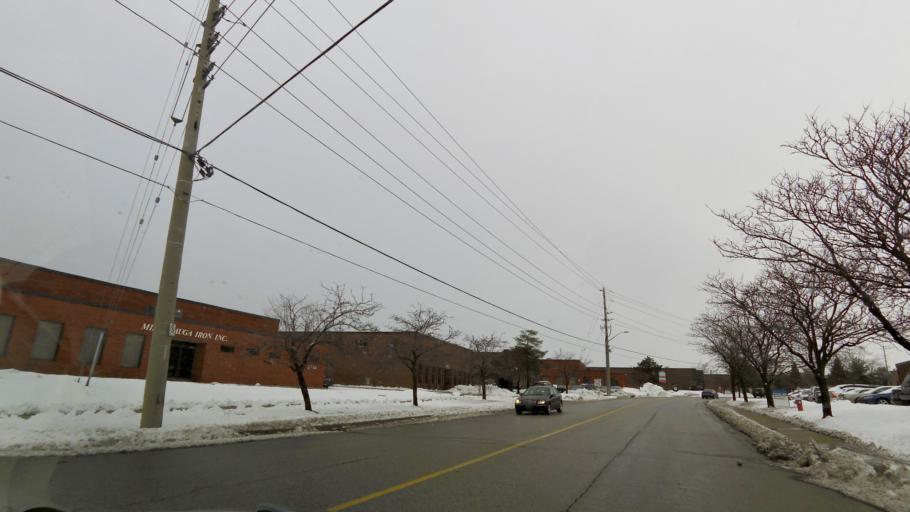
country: CA
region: Ontario
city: Mississauga
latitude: 43.6495
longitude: -79.6568
